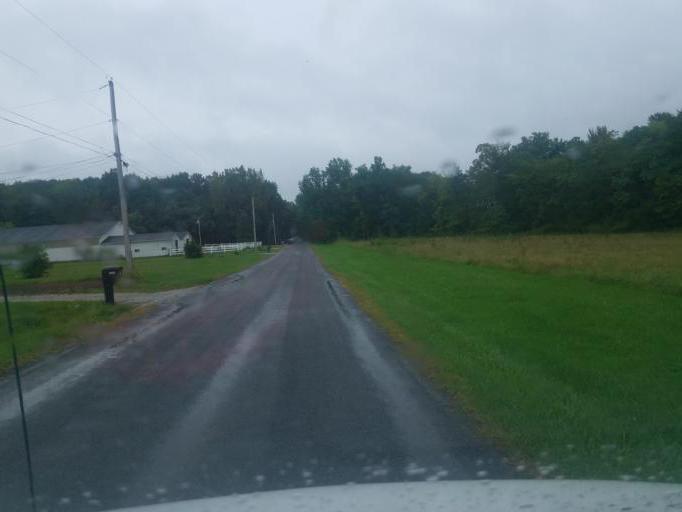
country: US
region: Ohio
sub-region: Medina County
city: Seville
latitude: 41.0291
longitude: -81.8148
